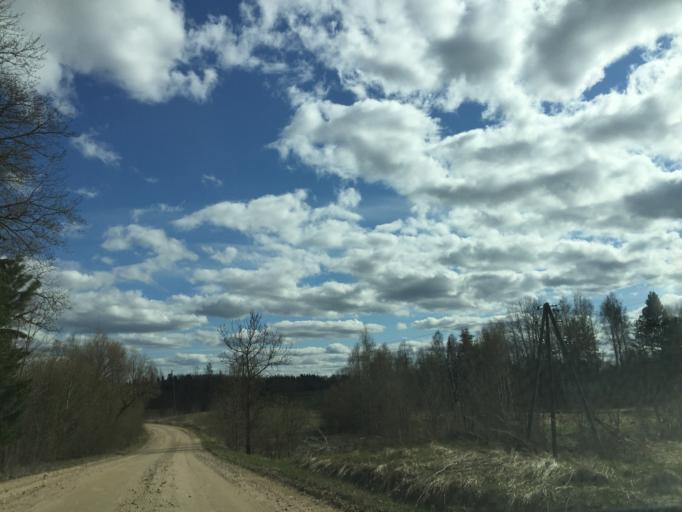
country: LV
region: Rezekne
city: Rezekne
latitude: 56.6492
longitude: 27.2866
